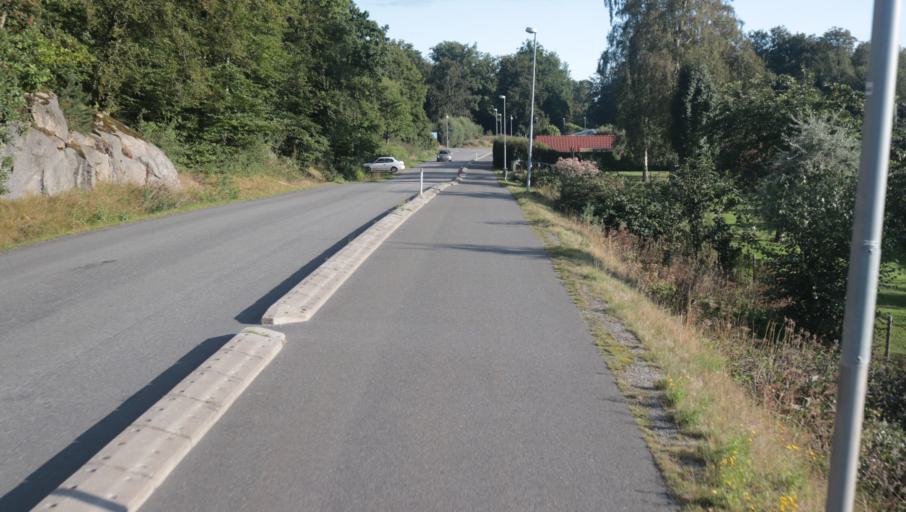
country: SE
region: Blekinge
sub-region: Karlshamns Kommun
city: Karlshamn
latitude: 56.1648
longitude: 14.8977
